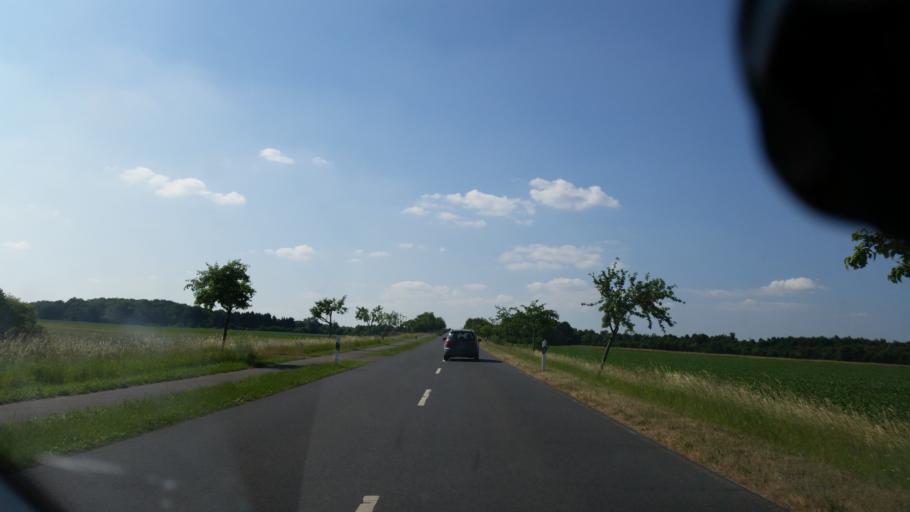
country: DE
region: Lower Saxony
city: Konigslutter am Elm
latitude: 52.3080
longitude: 10.7667
